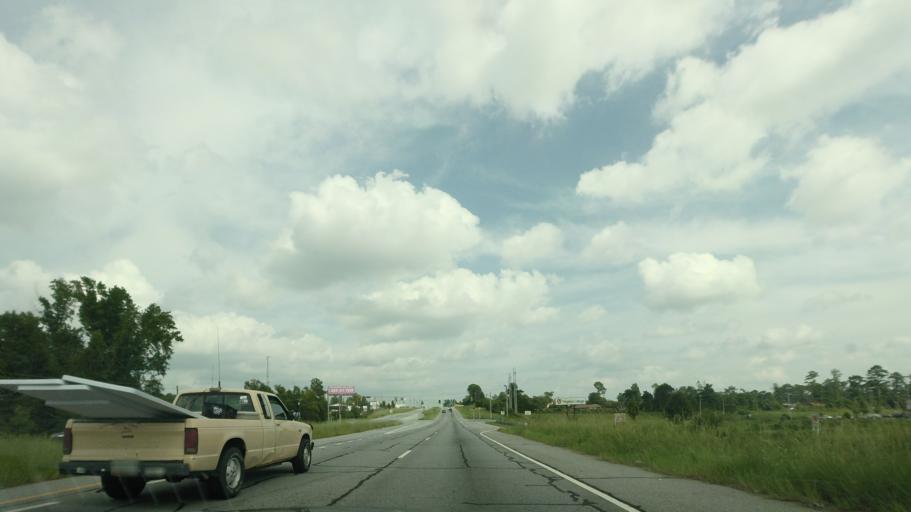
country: US
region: Georgia
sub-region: Bibb County
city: Macon
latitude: 32.8149
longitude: -83.6808
